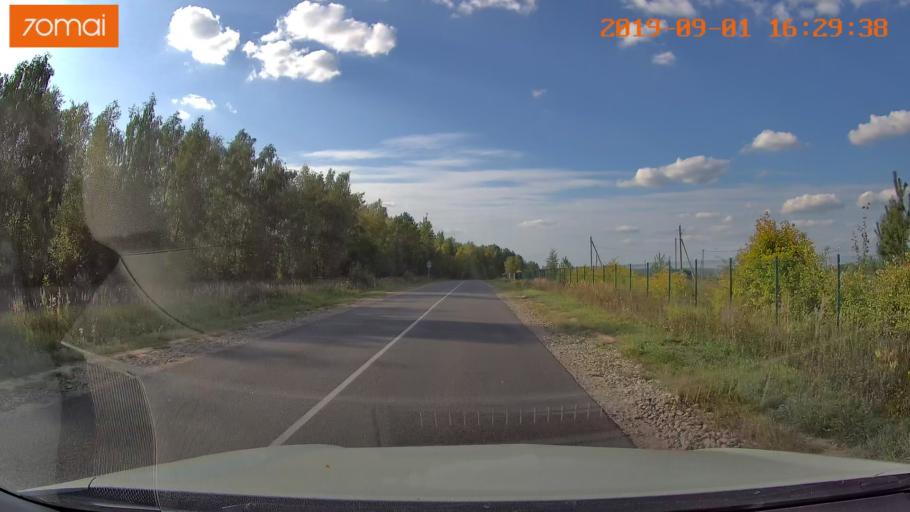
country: RU
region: Kaluga
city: Maloyaroslavets
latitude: 54.9375
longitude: 36.4634
